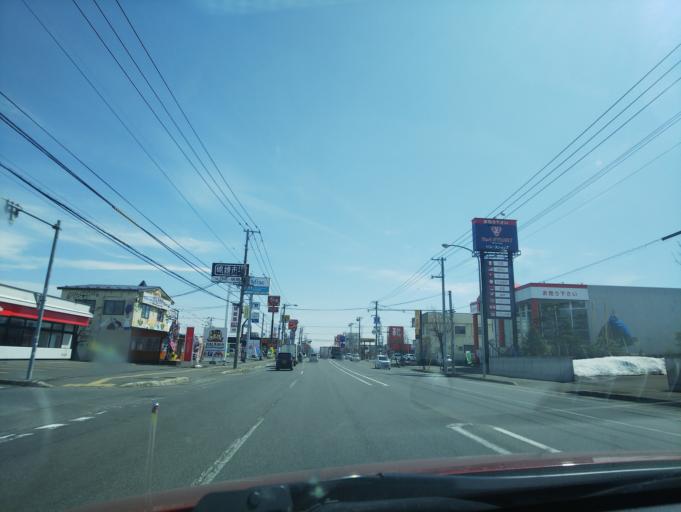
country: JP
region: Hokkaido
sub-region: Asahikawa-shi
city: Asahikawa
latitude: 43.7884
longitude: 142.4075
